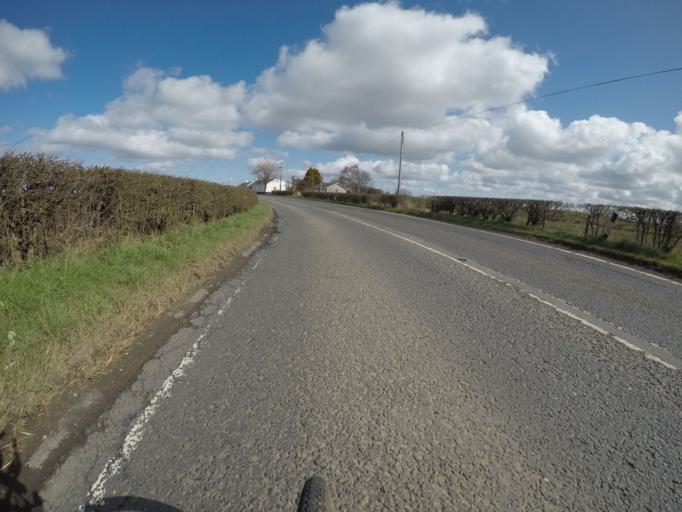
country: GB
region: Scotland
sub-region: East Ayrshire
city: Crosshouse
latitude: 55.5887
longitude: -4.5552
